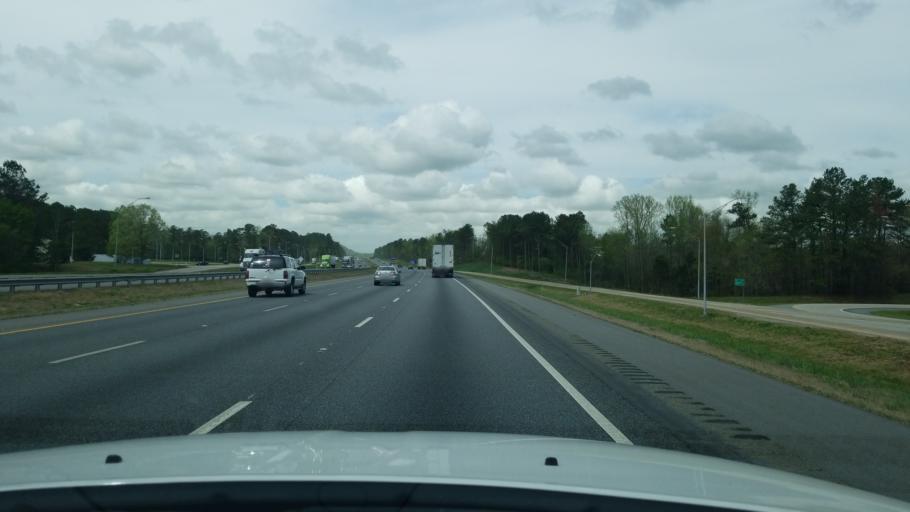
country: US
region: Georgia
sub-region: Catoosa County
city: Ringgold
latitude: 34.8796
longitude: -85.0492
